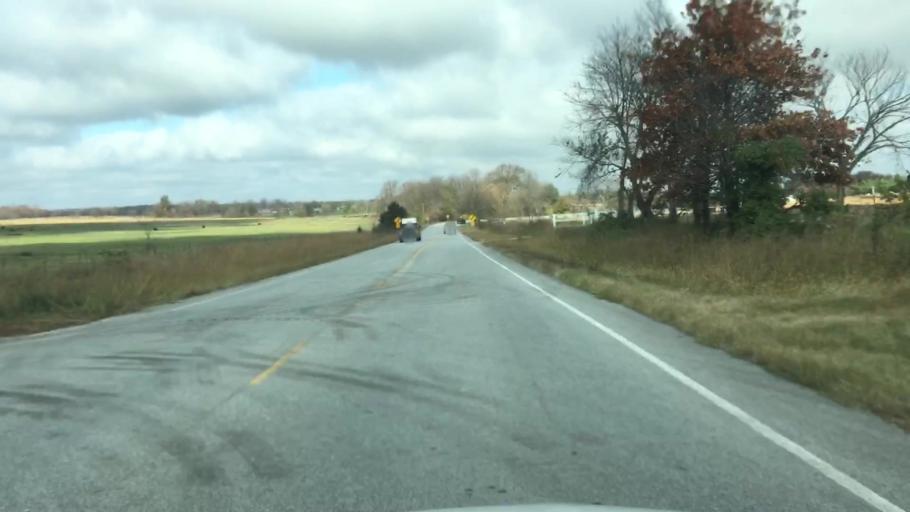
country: US
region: Arkansas
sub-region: Benton County
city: Centerton
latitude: 36.2834
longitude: -94.3501
